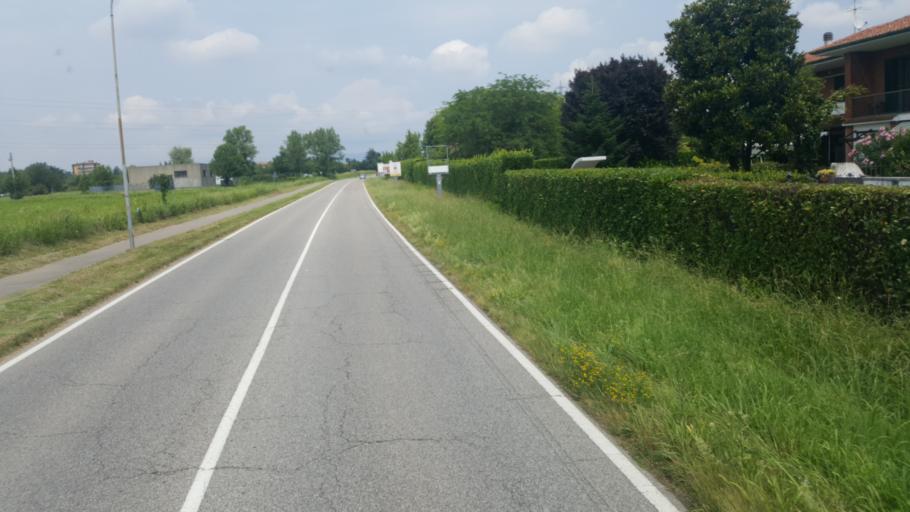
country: IT
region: Lombardy
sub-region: Provincia di Monza e Brianza
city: Burago di Molgora
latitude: 45.6008
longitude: 9.3789
